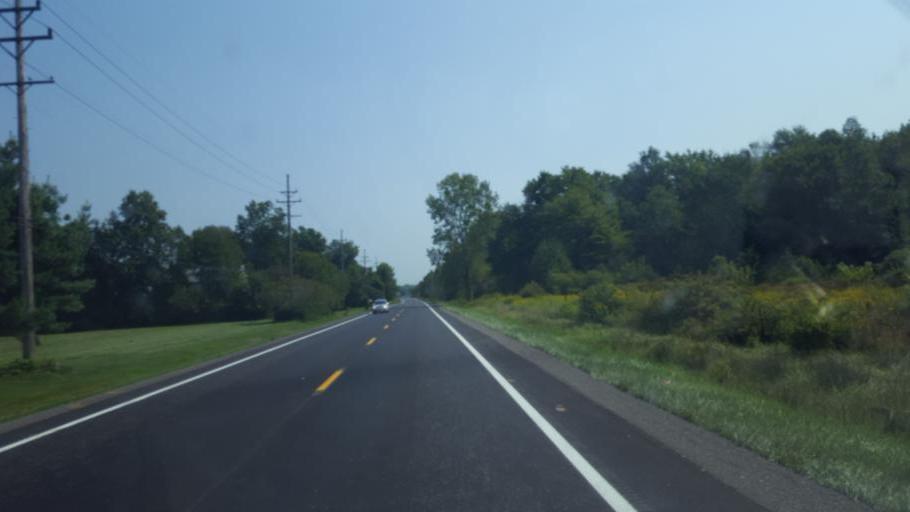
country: US
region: Ohio
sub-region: Ashtabula County
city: Orwell
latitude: 41.5345
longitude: -80.9068
